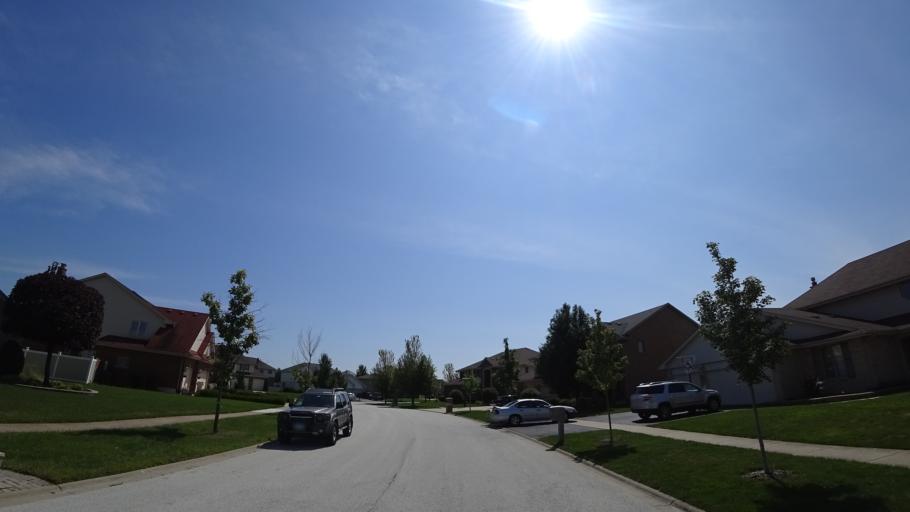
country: US
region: Illinois
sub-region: Cook County
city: Orland Hills
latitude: 41.5623
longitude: -87.8312
